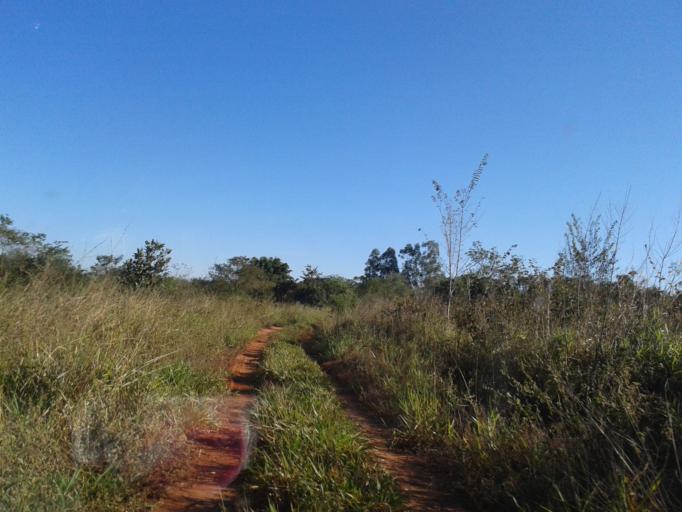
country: BR
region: Minas Gerais
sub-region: Santa Vitoria
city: Santa Vitoria
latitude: -19.0119
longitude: -50.3834
